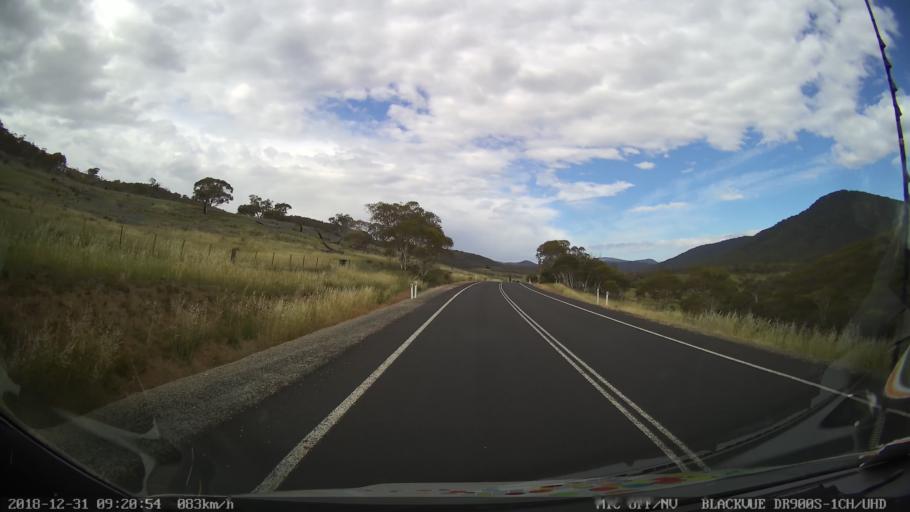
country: AU
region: New South Wales
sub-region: Snowy River
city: Jindabyne
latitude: -36.4247
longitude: 148.5684
